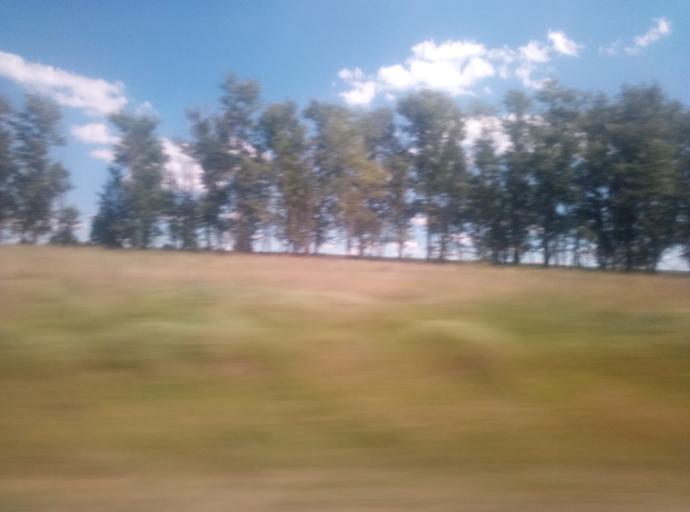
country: RU
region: Tula
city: Kireyevsk
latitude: 53.9419
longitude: 37.9486
